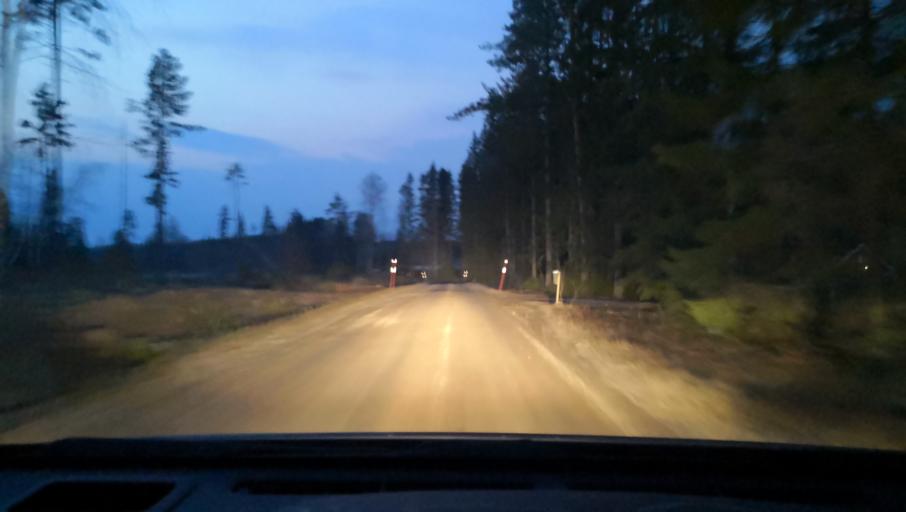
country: SE
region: OErebro
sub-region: Lindesbergs Kommun
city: Frovi
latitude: 59.5915
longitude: 15.4699
